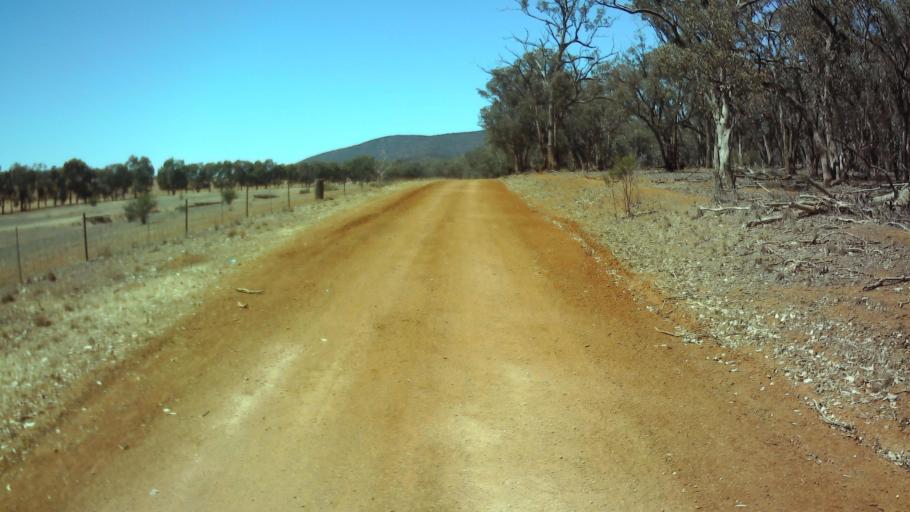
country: AU
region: New South Wales
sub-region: Weddin
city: Grenfell
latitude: -33.9505
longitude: 148.0845
